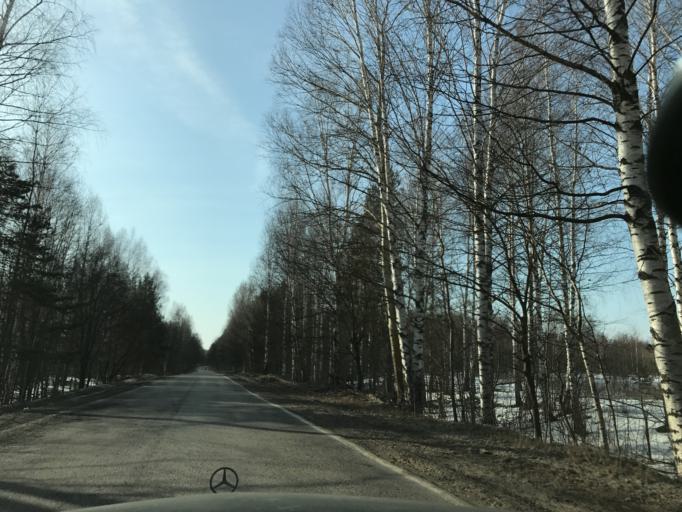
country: RU
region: Nizjnij Novgorod
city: Taremskoye
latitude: 55.9986
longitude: 42.8908
